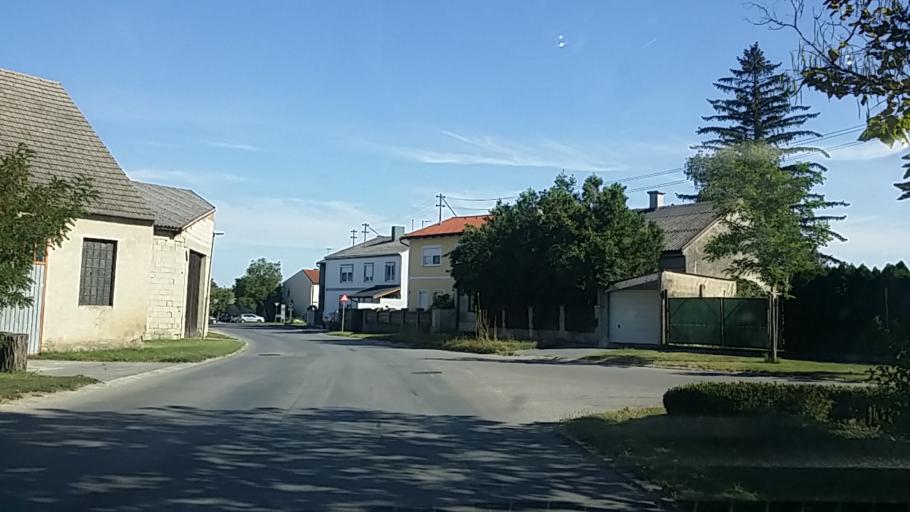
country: AT
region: Burgenland
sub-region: Politischer Bezirk Neusiedl am See
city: Pamhagen
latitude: 47.6996
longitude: 16.9092
